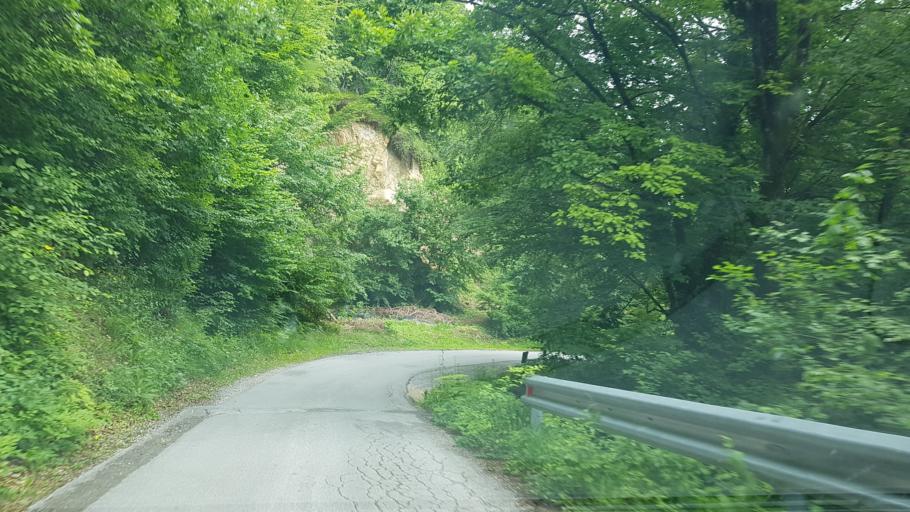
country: SI
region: Dobrna
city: Dobrna
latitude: 46.3509
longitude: 15.2377
